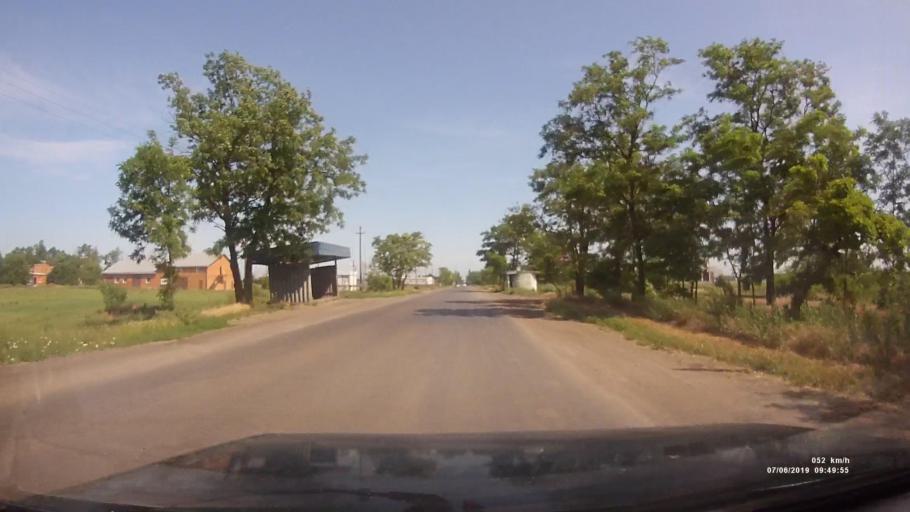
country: RU
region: Rostov
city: Azov
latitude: 47.0749
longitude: 39.4377
